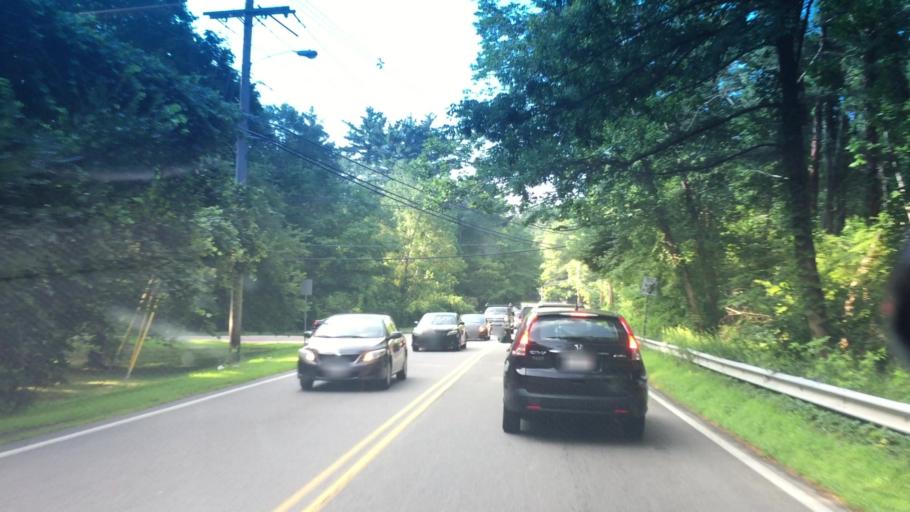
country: US
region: Massachusetts
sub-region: Norfolk County
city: Medfield
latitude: 42.1734
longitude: -71.2986
